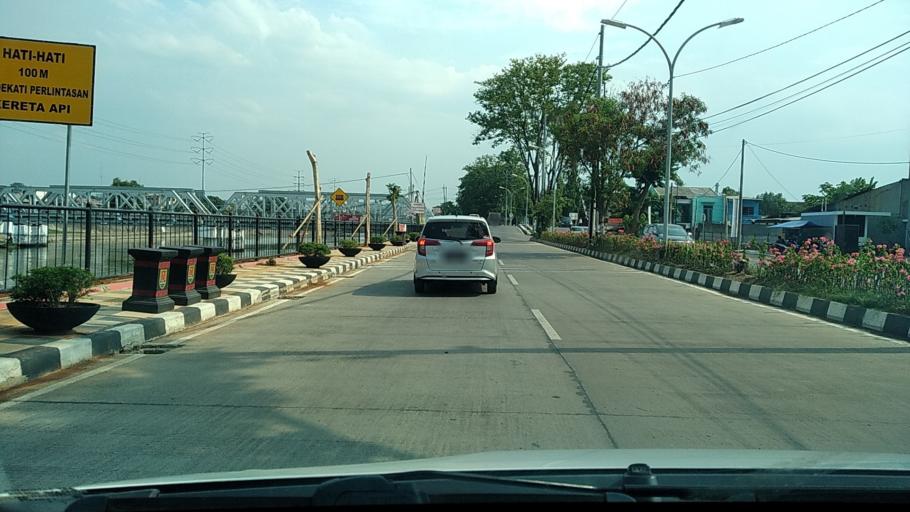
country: ID
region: Central Java
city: Semarang
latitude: -6.9765
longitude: 110.4010
